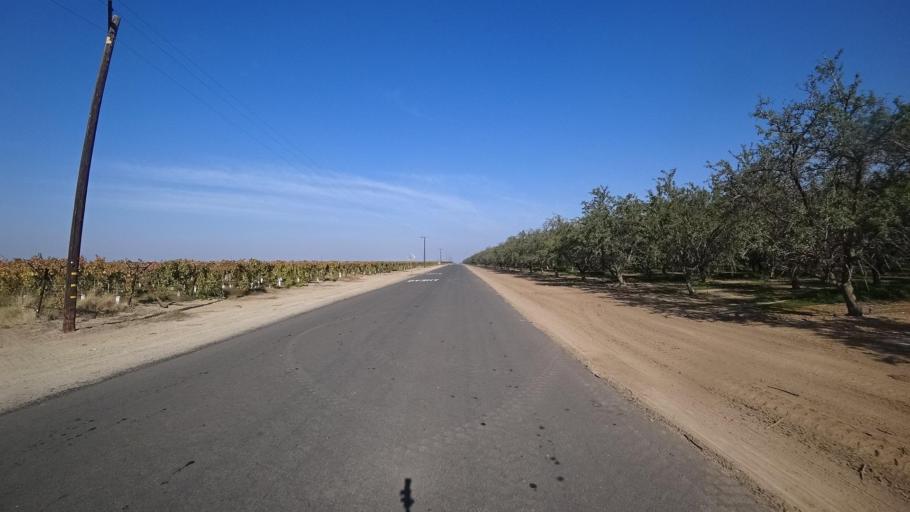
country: US
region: California
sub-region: Kern County
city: McFarland
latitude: 35.6471
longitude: -119.1867
